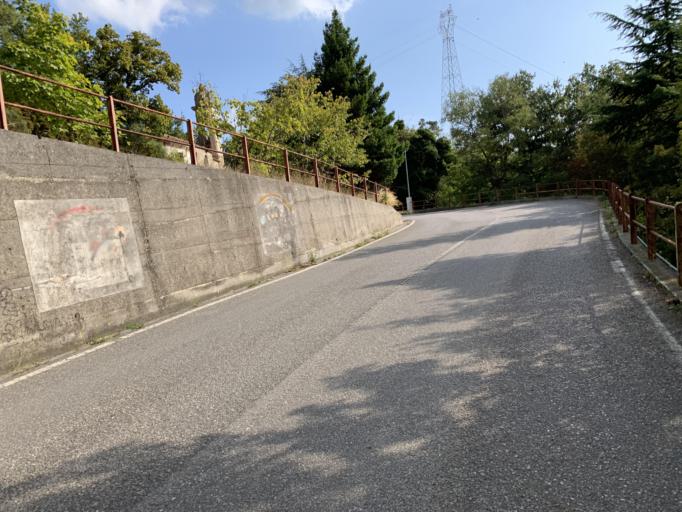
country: IT
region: Liguria
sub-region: Provincia di Savona
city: Feglino
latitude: 44.2169
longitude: 8.3112
